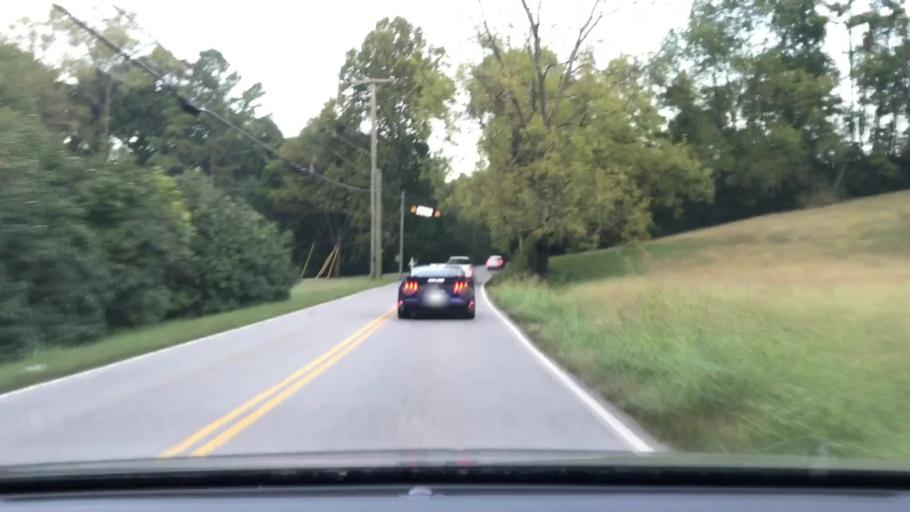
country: US
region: Tennessee
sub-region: Williamson County
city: Brentwood Estates
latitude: 36.0256
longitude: -86.7428
